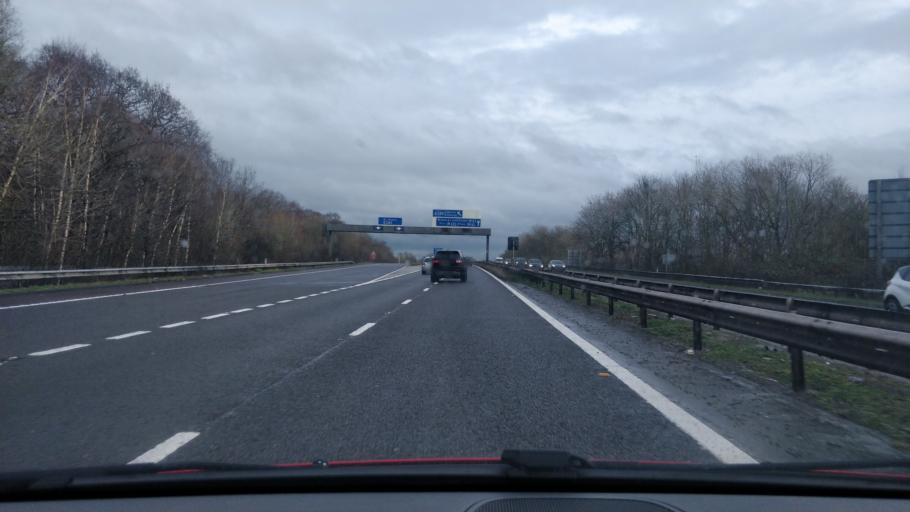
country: GB
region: England
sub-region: Knowsley
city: Kirkby
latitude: 53.4667
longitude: -2.8893
